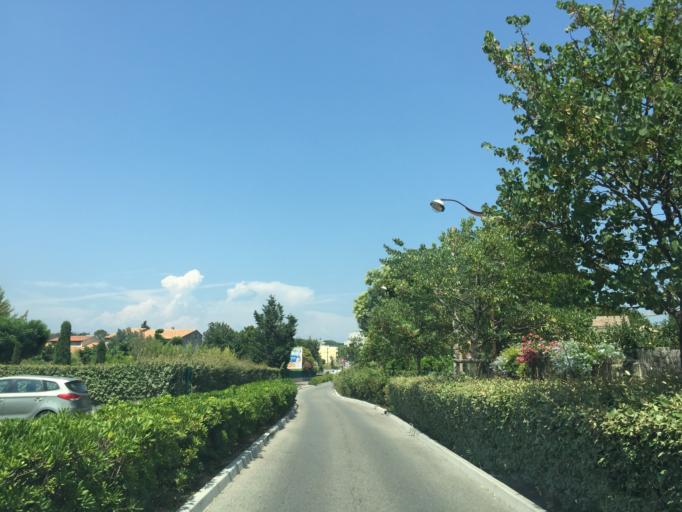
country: FR
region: Provence-Alpes-Cote d'Azur
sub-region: Departement du Var
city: Frejus
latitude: 43.4330
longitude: 6.7496
